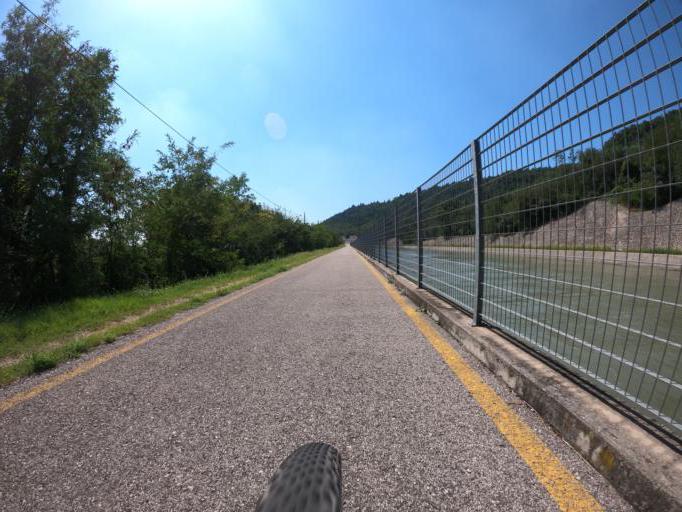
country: IT
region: Veneto
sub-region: Provincia di Verona
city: Volargne
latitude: 45.5540
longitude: 10.8235
